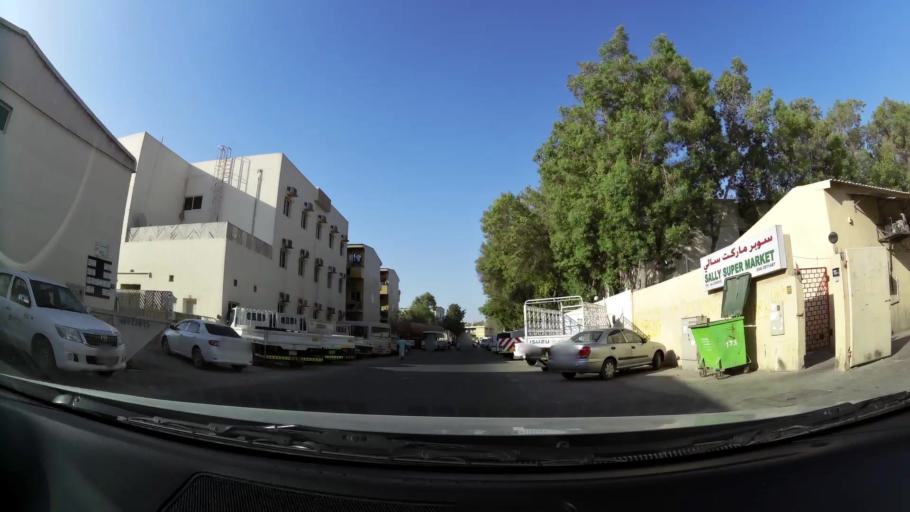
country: AE
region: Dubai
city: Dubai
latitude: 25.1352
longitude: 55.2558
